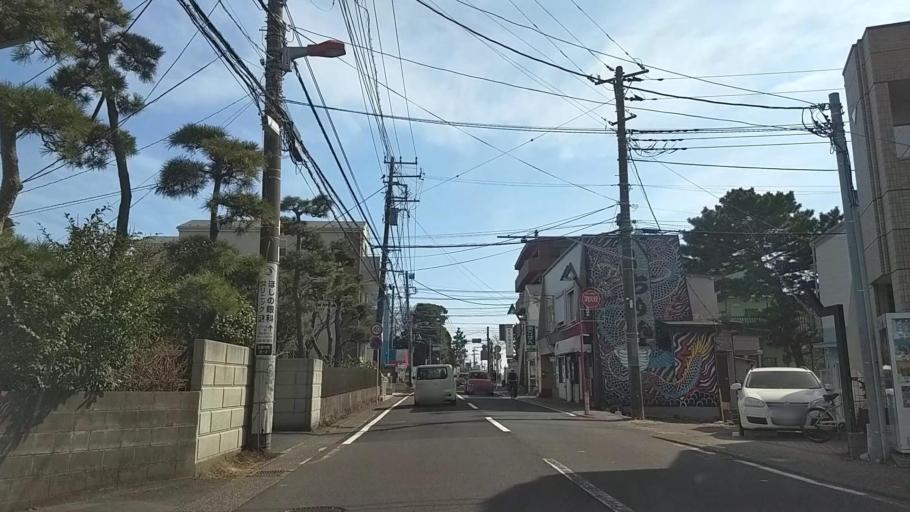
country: JP
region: Kanagawa
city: Fujisawa
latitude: 35.3280
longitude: 139.4527
